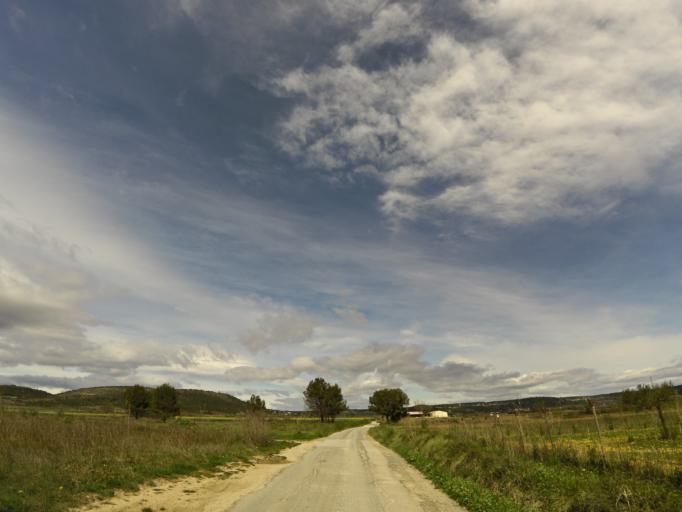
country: FR
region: Languedoc-Roussillon
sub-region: Departement du Gard
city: Calvisson
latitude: 43.7940
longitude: 4.2045
